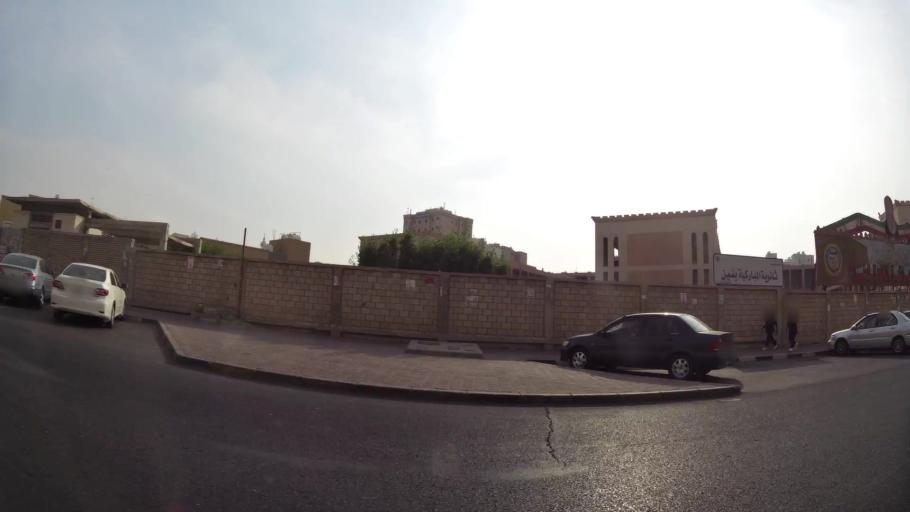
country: KW
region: Al Farwaniyah
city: Al Farwaniyah
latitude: 29.2727
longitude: 47.9653
